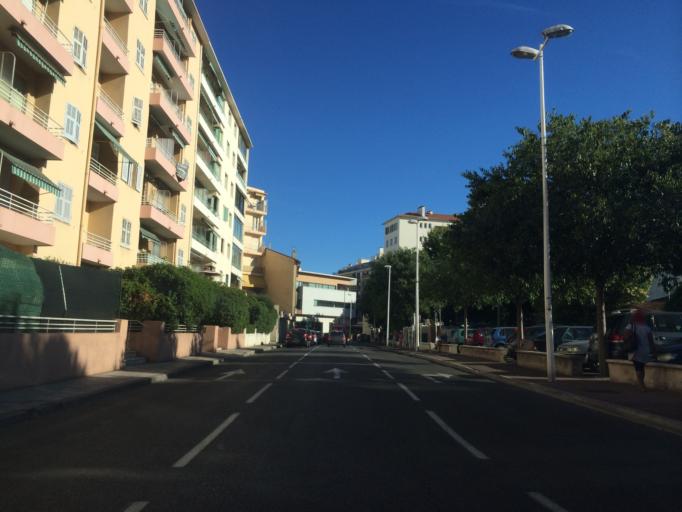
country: FR
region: Provence-Alpes-Cote d'Azur
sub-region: Departement des Alpes-Maritimes
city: Antibes
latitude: 43.5805
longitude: 7.1186
